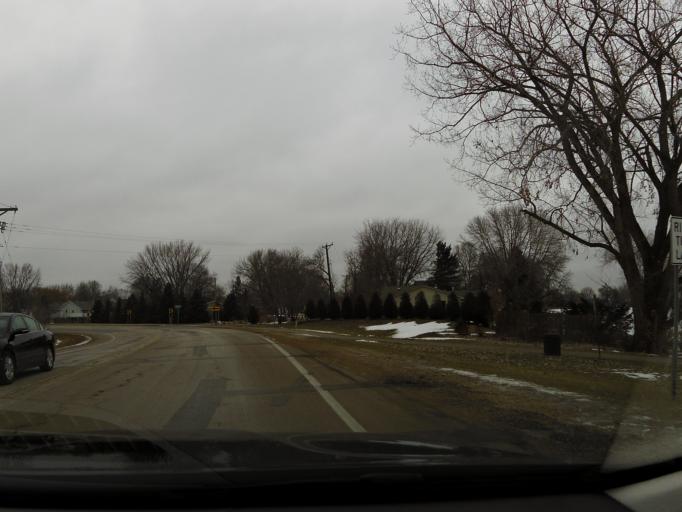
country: US
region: Minnesota
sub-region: Carver County
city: Waconia
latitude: 44.8541
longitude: -93.7963
